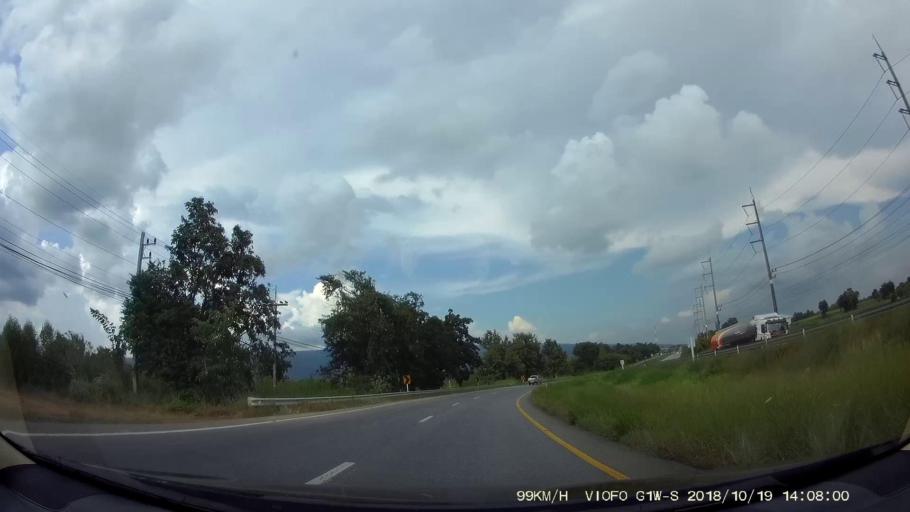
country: TH
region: Chaiyaphum
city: Chaiyaphum
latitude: 15.9018
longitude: 102.1197
